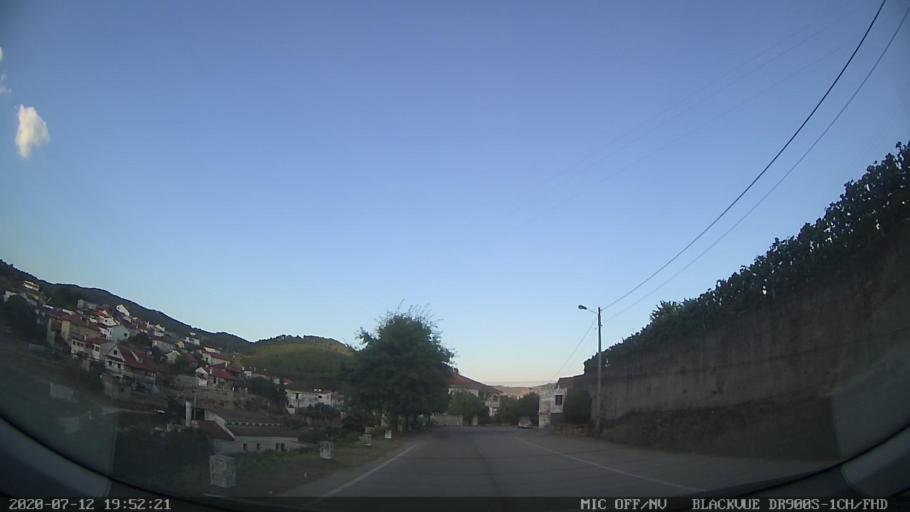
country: PT
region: Viseu
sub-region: Sao Joao da Pesqueira
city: Sao Joao da Pesqueira
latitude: 41.2505
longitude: -7.4335
